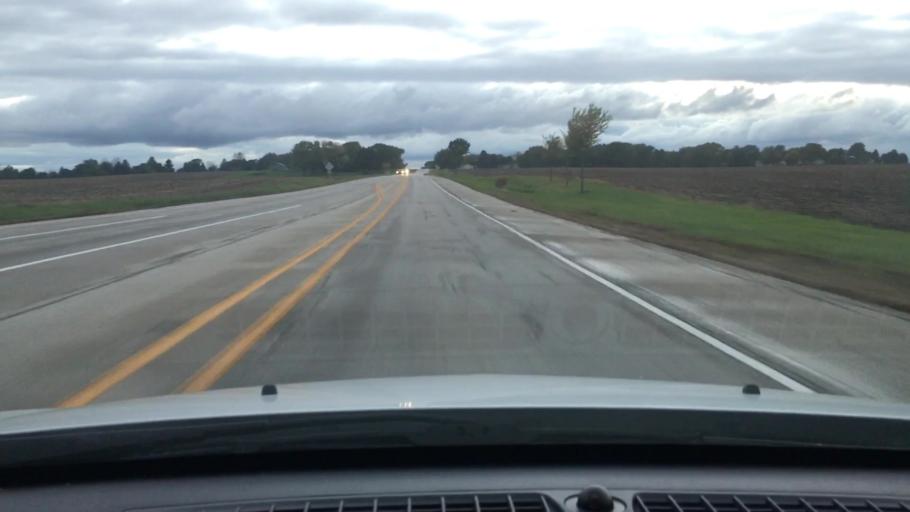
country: US
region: Illinois
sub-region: DeKalb County
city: Malta
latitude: 41.9362
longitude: -88.8129
